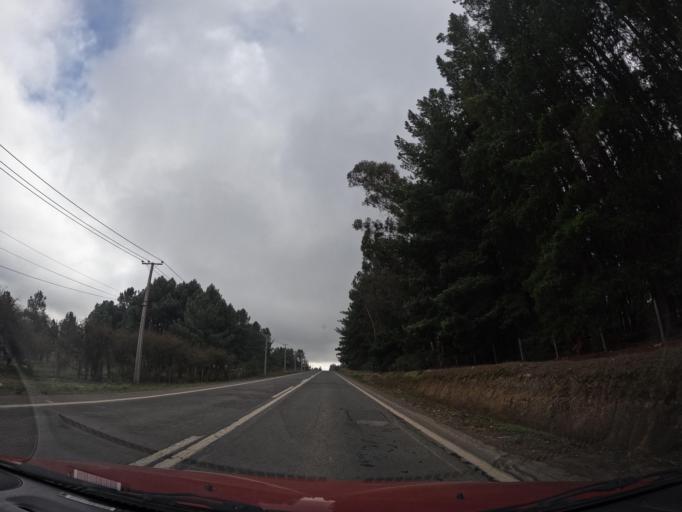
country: CL
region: Maule
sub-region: Provincia de Cauquenes
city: Cauquenes
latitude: -36.2576
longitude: -72.5482
